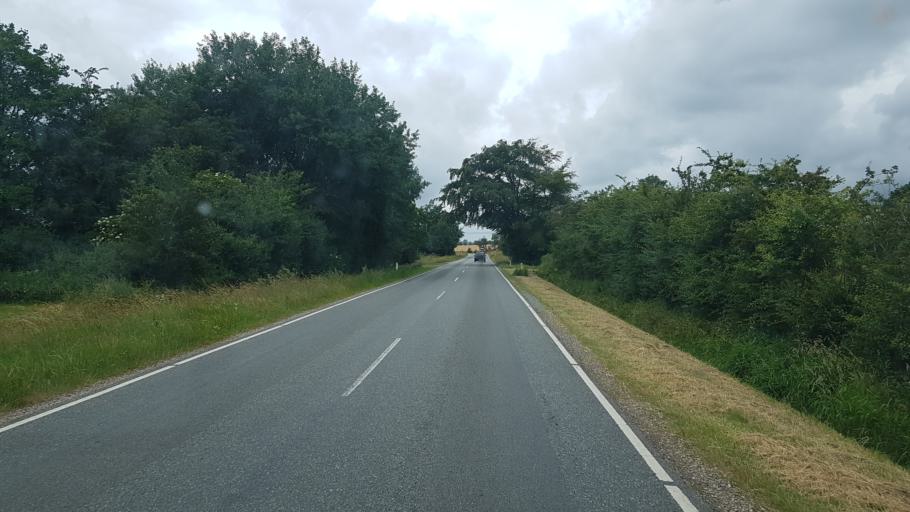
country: DK
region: South Denmark
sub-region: Vejen Kommune
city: Vejen
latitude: 55.4367
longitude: 9.1859
